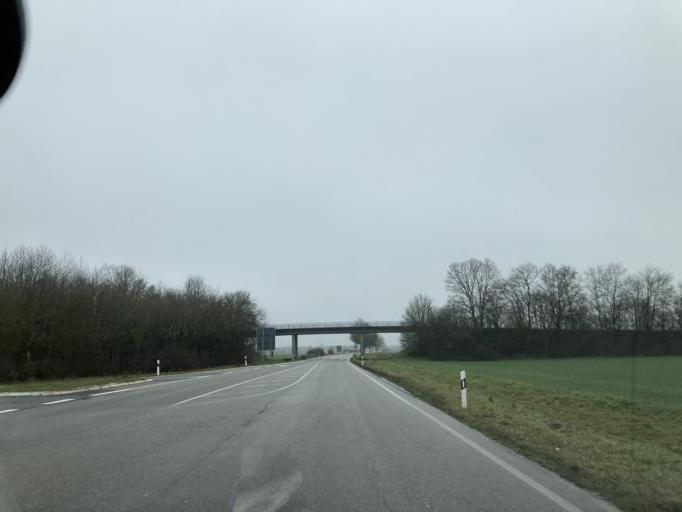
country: DE
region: Baden-Wuerttemberg
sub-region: Freiburg Region
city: Neuenburg am Rhein
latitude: 47.8160
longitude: 7.5871
